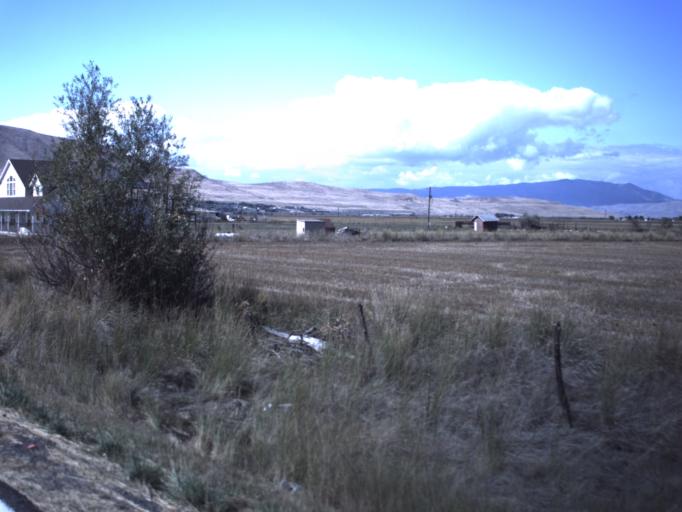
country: US
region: Utah
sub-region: Utah County
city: Benjamin
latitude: 40.0979
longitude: -111.7637
